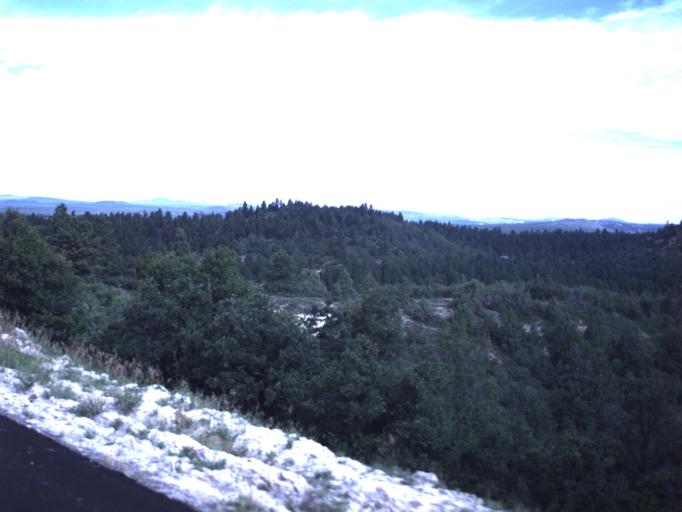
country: US
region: Utah
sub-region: Garfield County
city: Panguitch
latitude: 37.4972
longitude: -112.5345
